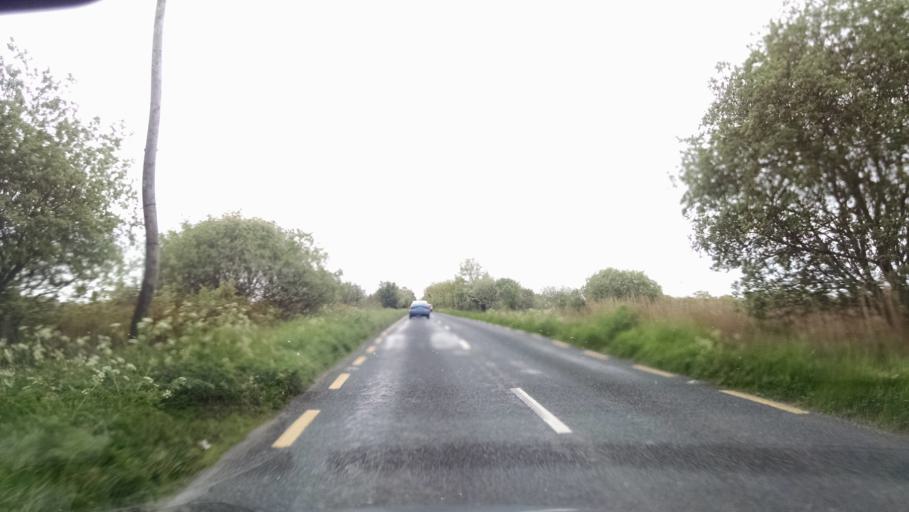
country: IE
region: Connaught
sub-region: County Galway
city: Claregalway
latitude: 53.3956
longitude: -9.0173
